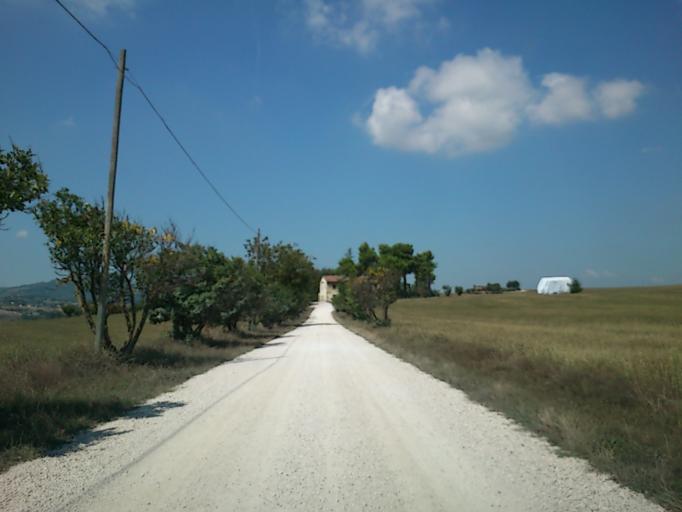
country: IT
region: The Marches
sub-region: Provincia di Pesaro e Urbino
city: Lucrezia
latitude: 43.7774
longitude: 12.9295
